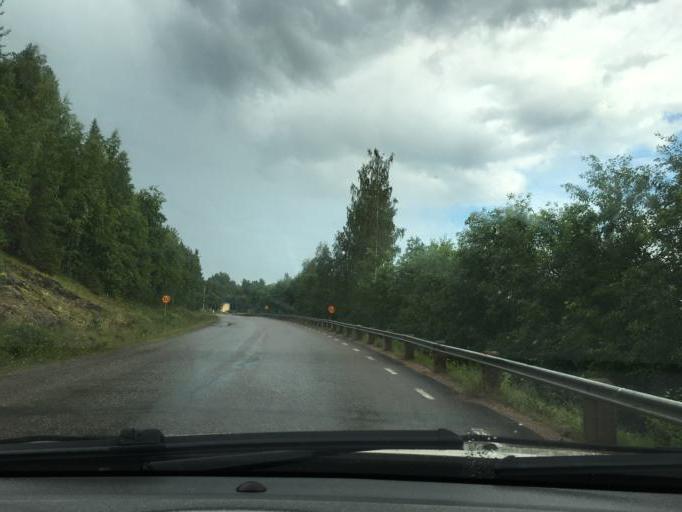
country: SE
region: Norrbotten
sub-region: Kalix Kommun
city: Rolfs
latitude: 65.9329
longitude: 22.8929
